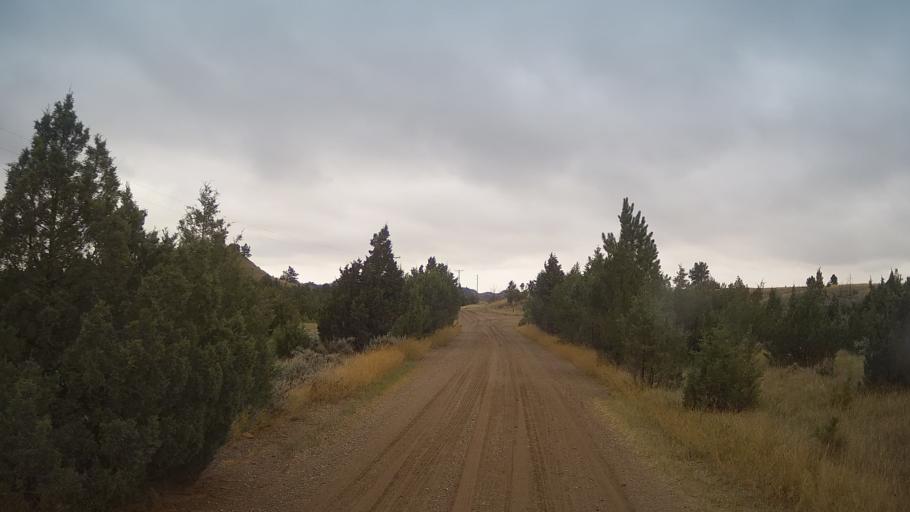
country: US
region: Montana
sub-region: Dawson County
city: Glendive
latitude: 47.0449
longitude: -104.6769
